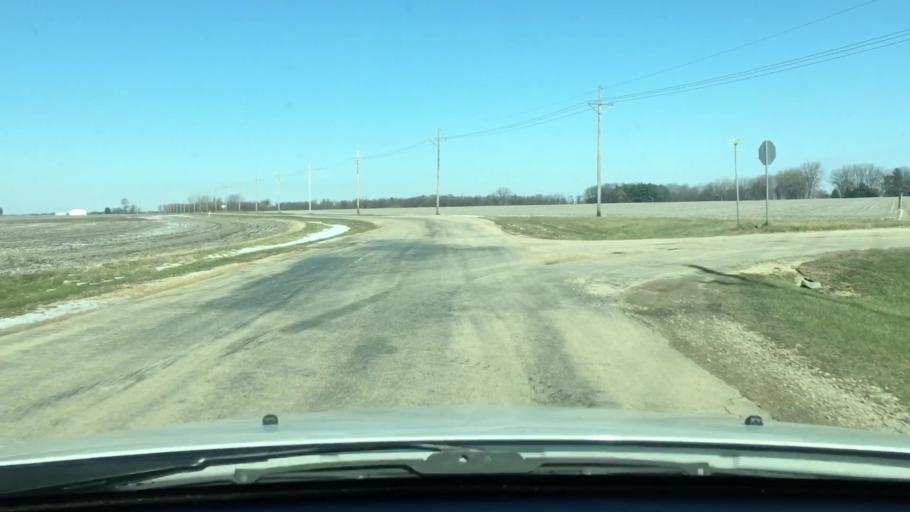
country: US
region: Illinois
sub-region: Ogle County
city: Hillcrest
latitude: 41.9783
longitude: -89.0008
